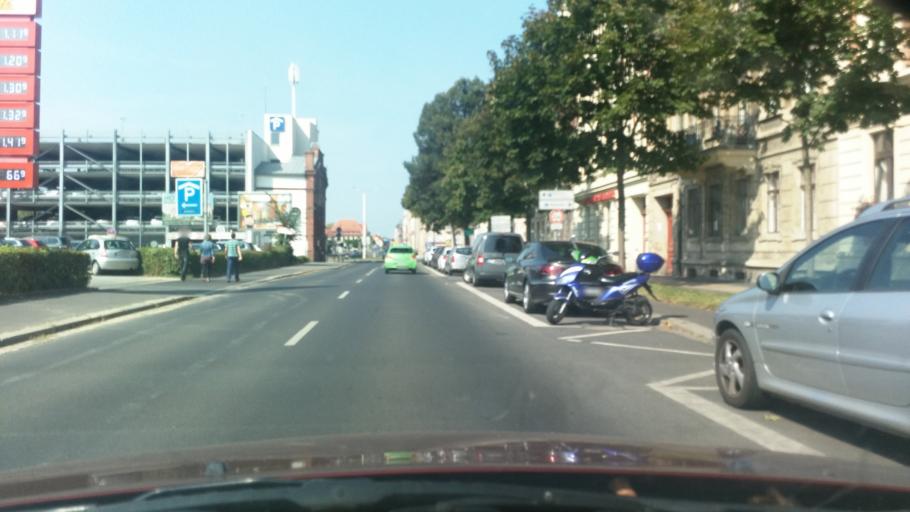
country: DE
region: Saxony
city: Goerlitz
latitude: 51.1462
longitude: 14.9837
